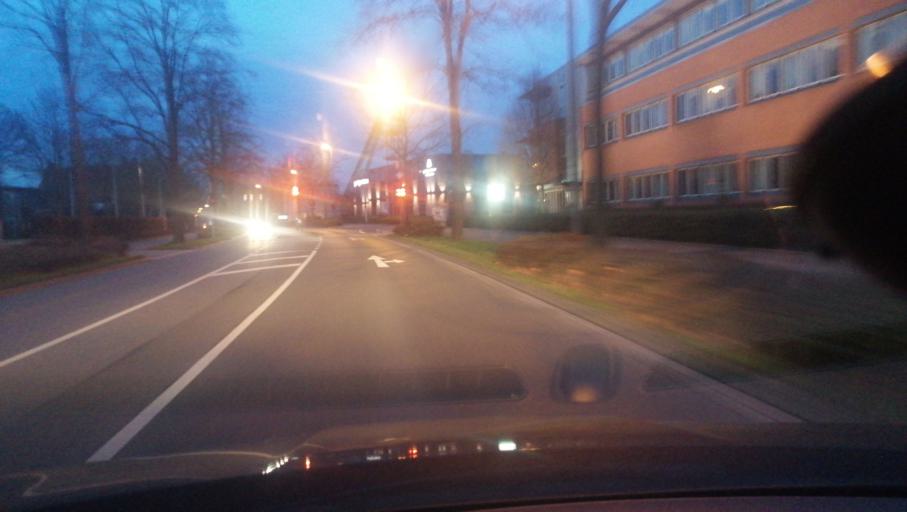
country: DE
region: North Rhine-Westphalia
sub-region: Regierungsbezirk Arnsberg
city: Dortmund
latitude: 51.5354
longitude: 7.4169
